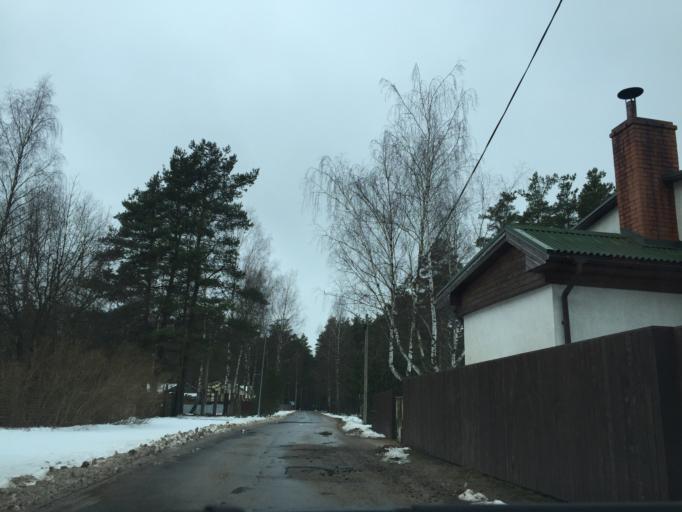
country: LV
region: Garkalne
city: Garkalne
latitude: 57.0415
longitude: 24.4312
